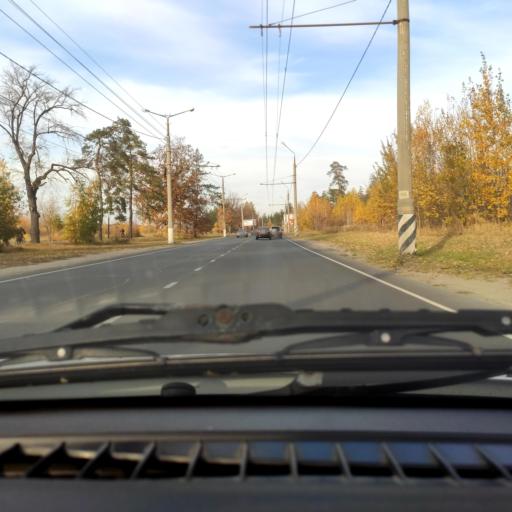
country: RU
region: Samara
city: Tol'yatti
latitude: 53.4862
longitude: 49.3817
